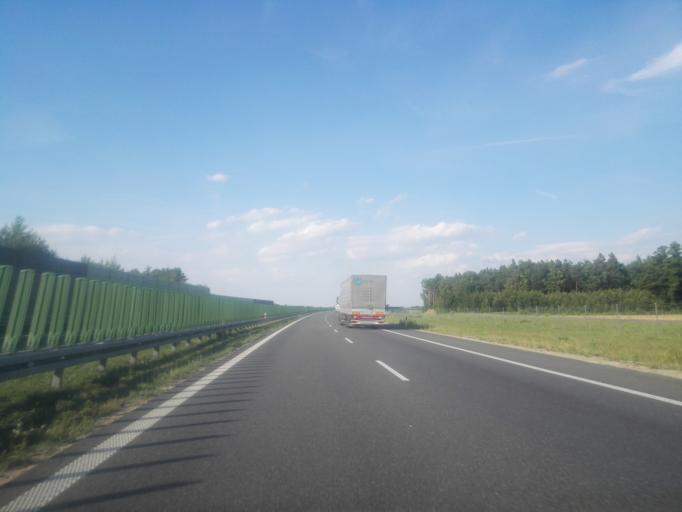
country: PL
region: Lower Silesian Voivodeship
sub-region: Powiat olesnicki
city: Miedzyborz
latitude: 51.2943
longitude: 17.5821
